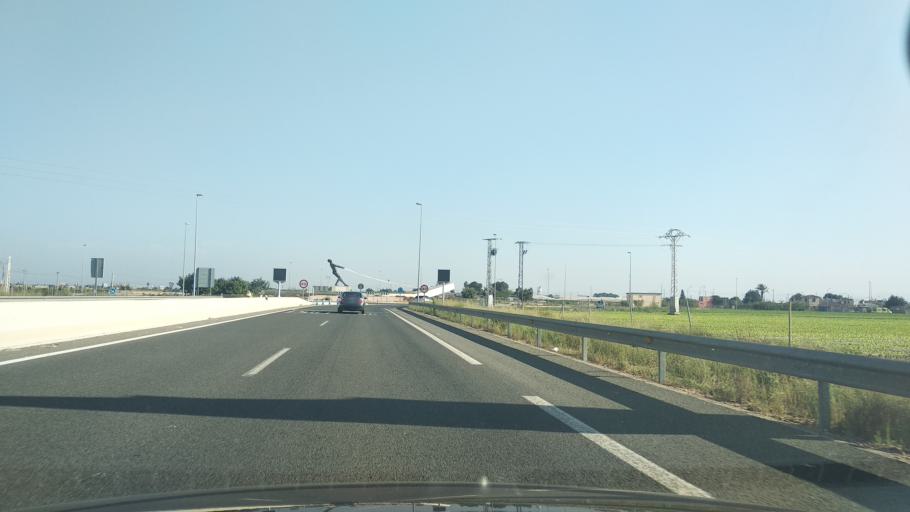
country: ES
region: Murcia
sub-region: Murcia
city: San Javier
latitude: 37.8226
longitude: -0.8506
